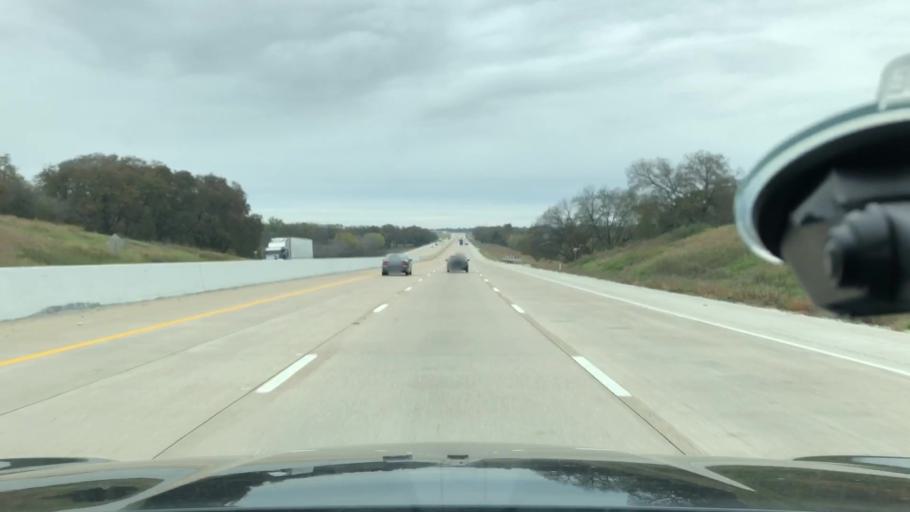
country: US
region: Texas
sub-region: Ellis County
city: Italy
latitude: 32.2222
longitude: -96.8869
